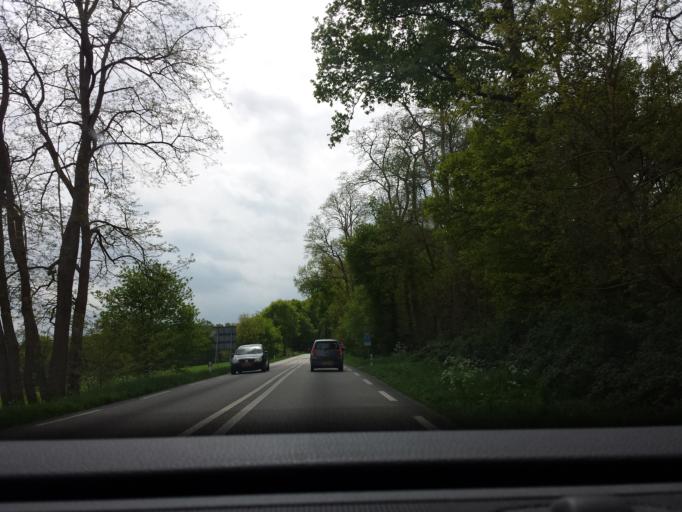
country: NL
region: Gelderland
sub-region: Gemeente Montferland
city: s-Heerenberg
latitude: 51.8961
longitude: 6.2574
